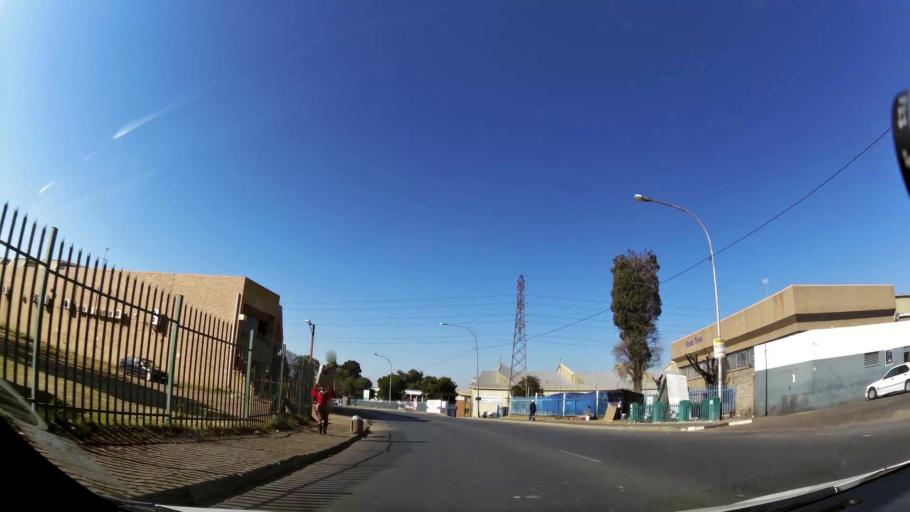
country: ZA
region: Gauteng
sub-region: Ekurhuleni Metropolitan Municipality
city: Germiston
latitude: -26.2055
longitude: 28.1167
